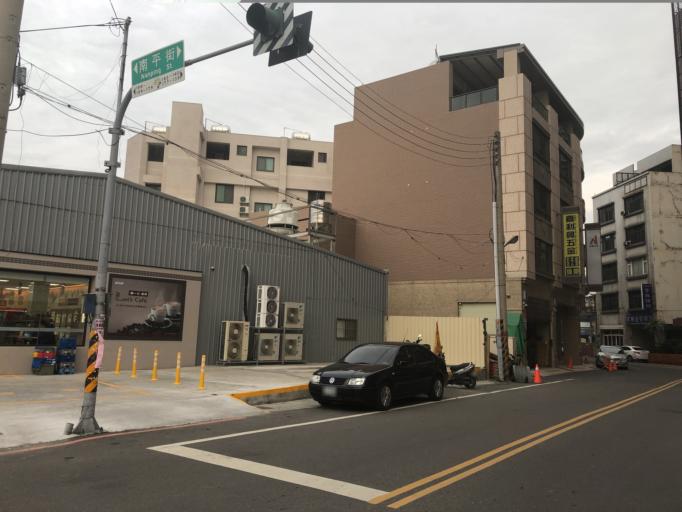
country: TW
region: Taiwan
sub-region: Changhua
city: Chang-hua
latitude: 23.9668
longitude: 120.5657
